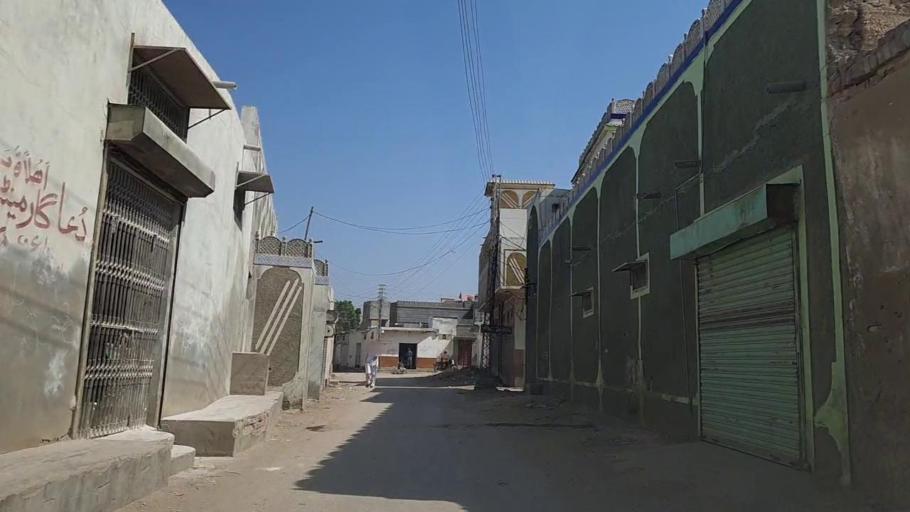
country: PK
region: Sindh
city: Naukot
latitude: 24.8612
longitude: 69.4039
